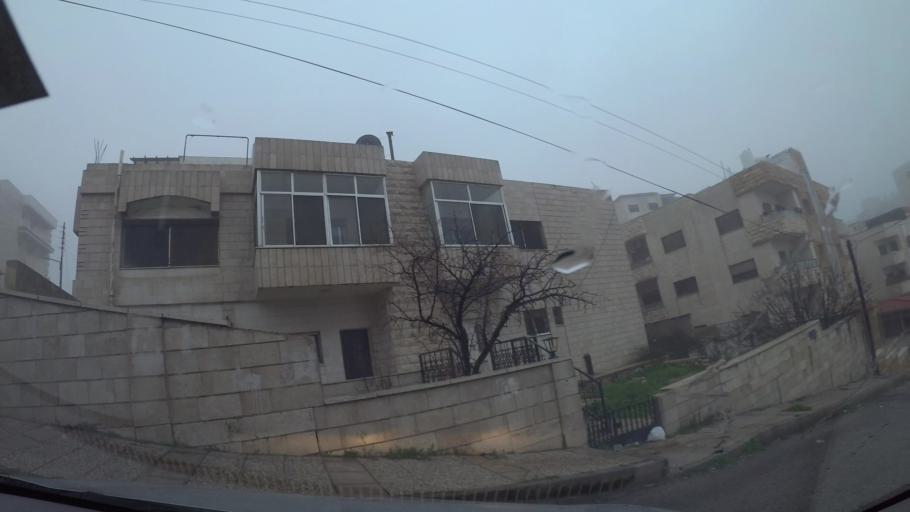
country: JO
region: Amman
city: Al Jubayhah
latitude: 32.0095
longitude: 35.8837
